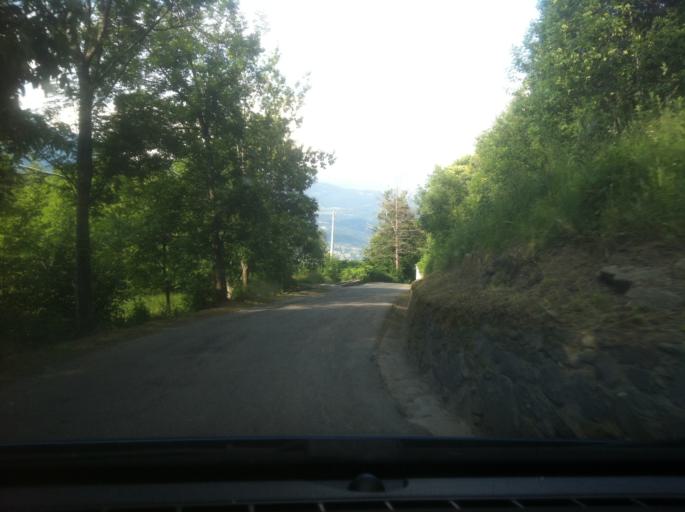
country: IT
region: Aosta Valley
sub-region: Valle d'Aosta
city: Saint Marcel
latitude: 45.7250
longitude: 7.4618
